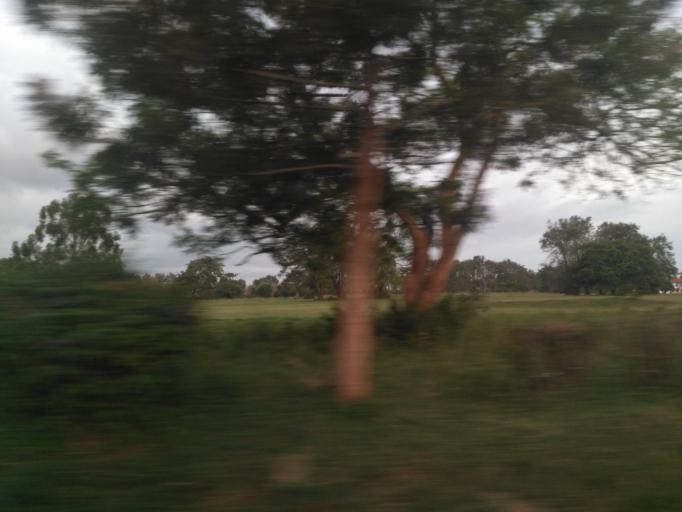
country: UG
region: Eastern Region
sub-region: Jinja District
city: Jinja
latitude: 0.4245
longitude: 33.1978
